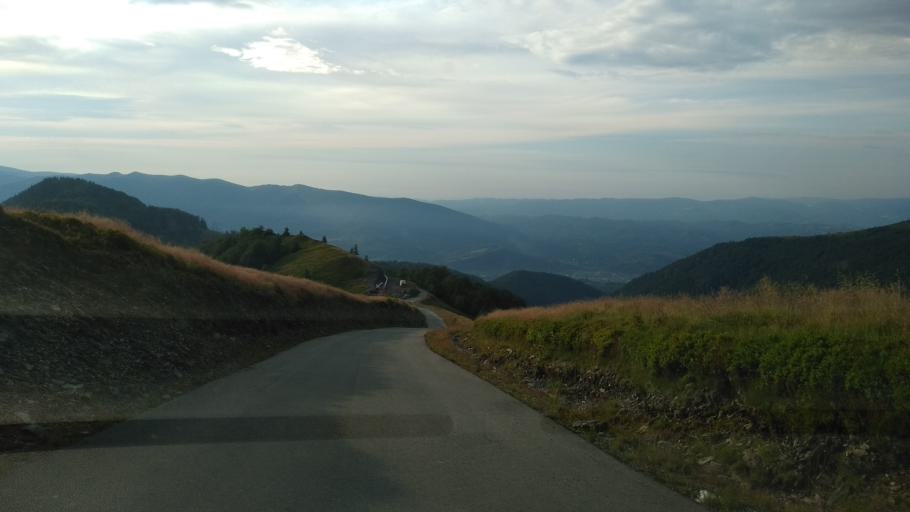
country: RO
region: Hunedoara
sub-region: Municipiul  Vulcan
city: Jiu-Paroseni
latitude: 45.3145
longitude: 23.3055
